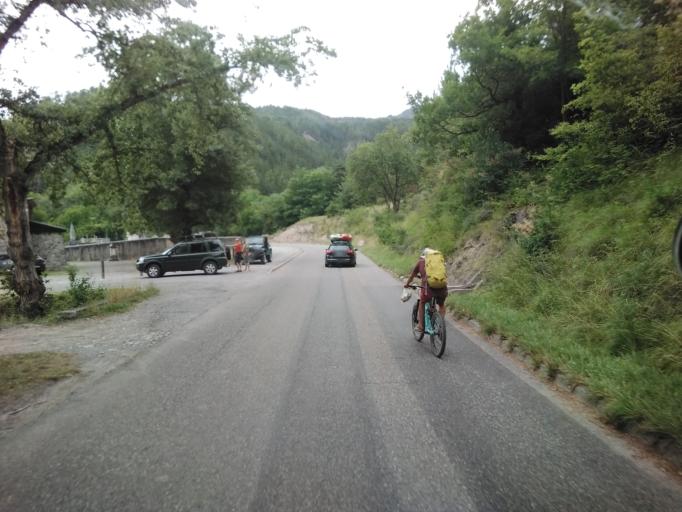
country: FR
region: Provence-Alpes-Cote d'Azur
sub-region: Departement des Alpes-de-Haute-Provence
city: Seyne-les-Alpes
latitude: 44.4643
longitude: 6.3618
